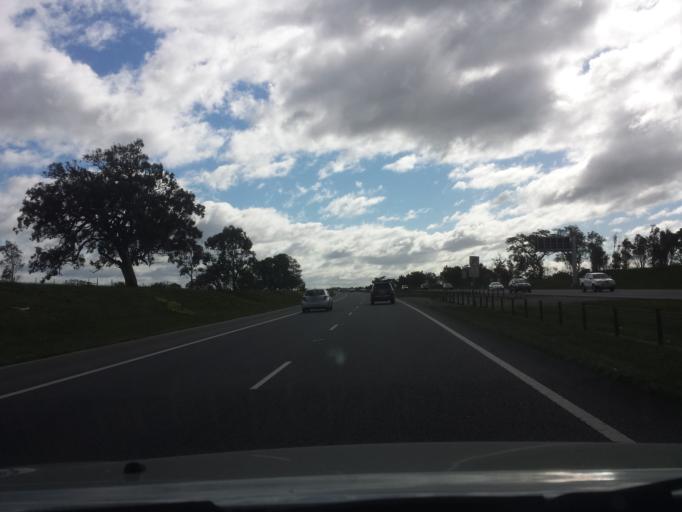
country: AU
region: Victoria
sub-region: Hume
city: Craigieburn
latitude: -37.6197
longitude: 144.9911
